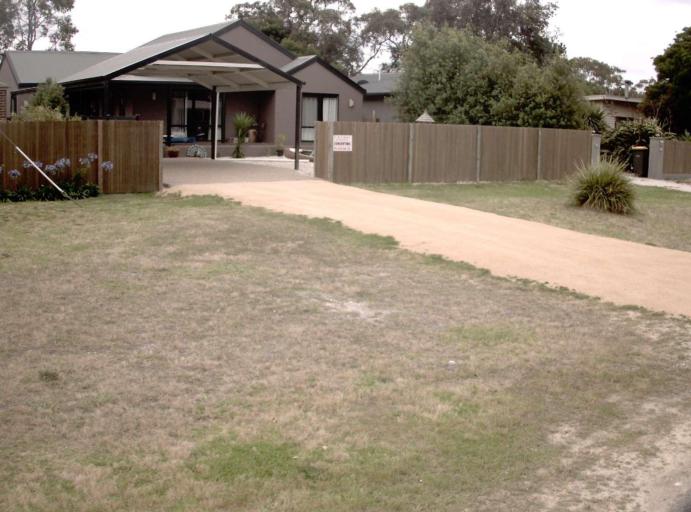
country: AU
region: Victoria
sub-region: East Gippsland
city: Bairnsdale
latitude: -38.0560
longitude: 147.5709
